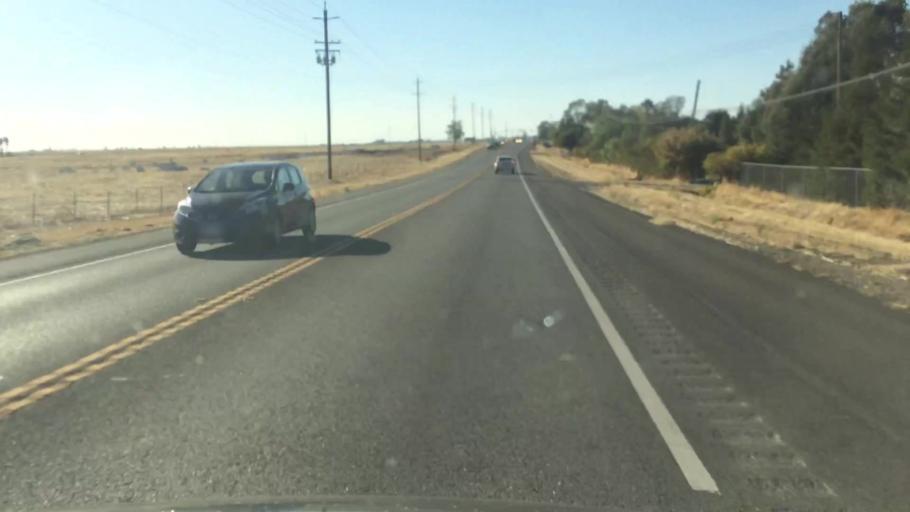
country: US
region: California
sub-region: Sacramento County
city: Wilton
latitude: 38.5009
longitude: -121.2182
